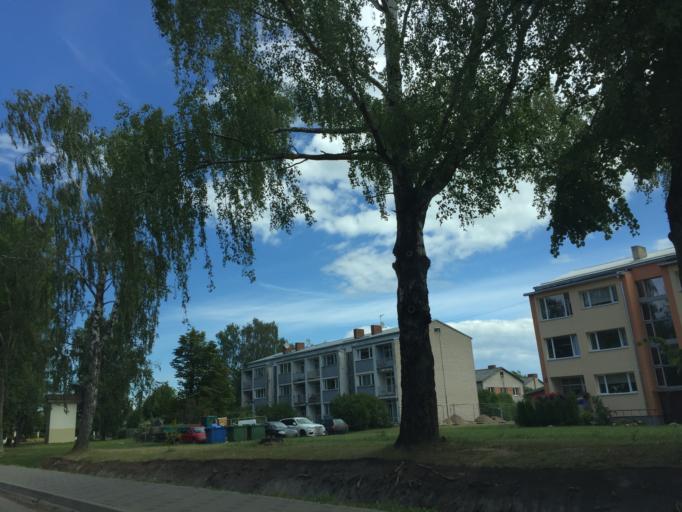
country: LV
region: Saulkrastu
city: Saulkrasti
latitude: 57.3160
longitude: 24.4152
